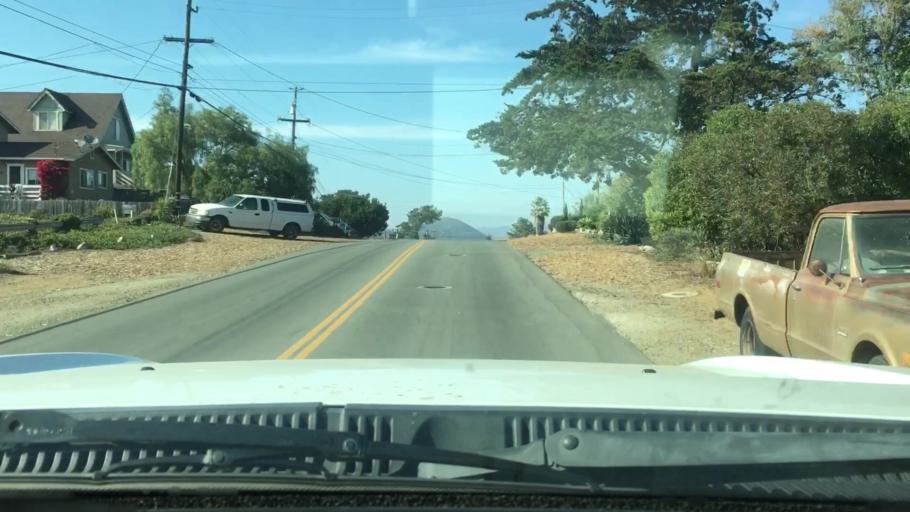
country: US
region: California
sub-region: San Luis Obispo County
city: Los Osos
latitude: 35.3180
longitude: -120.8311
